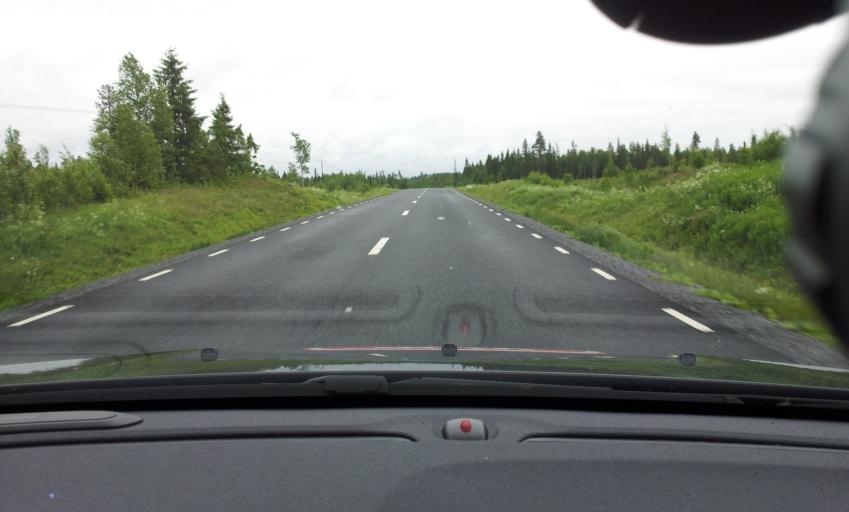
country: SE
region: Jaemtland
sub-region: Stroemsunds Kommun
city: Stroemsund
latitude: 63.6513
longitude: 15.1643
